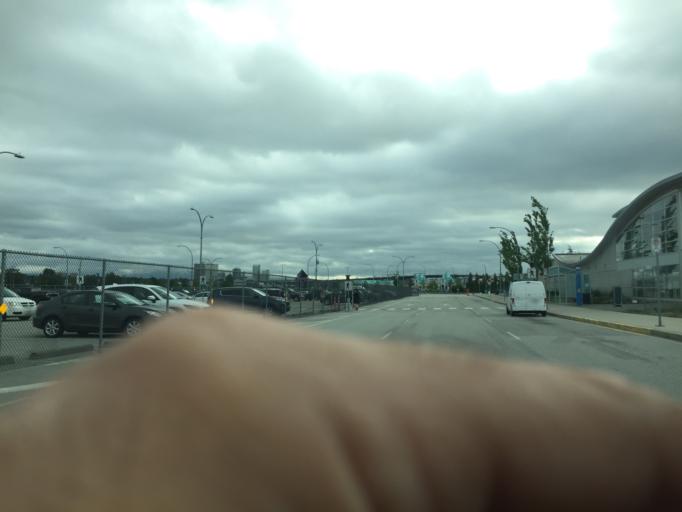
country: CA
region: British Columbia
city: Richmond
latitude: 49.1969
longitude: -123.1475
